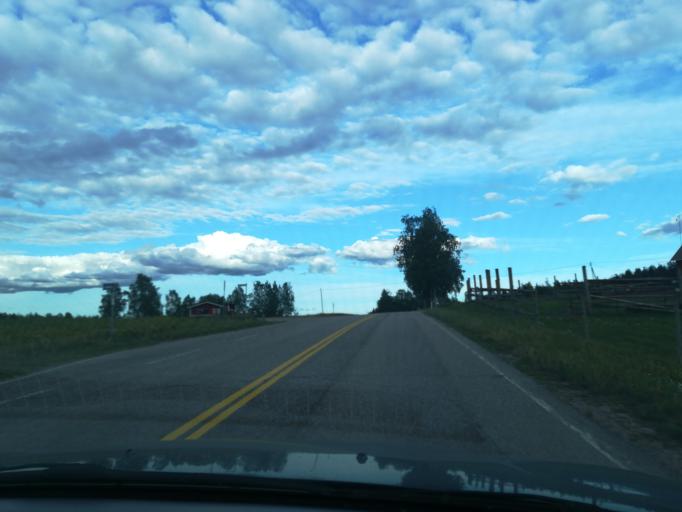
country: FI
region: Southern Savonia
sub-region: Mikkeli
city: Puumala
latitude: 61.5680
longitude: 28.0746
